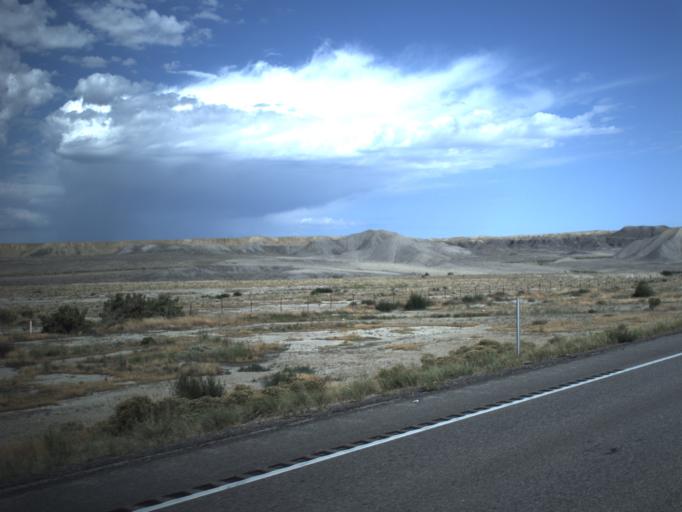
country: US
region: Utah
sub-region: Carbon County
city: East Carbon City
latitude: 39.3275
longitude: -110.3674
